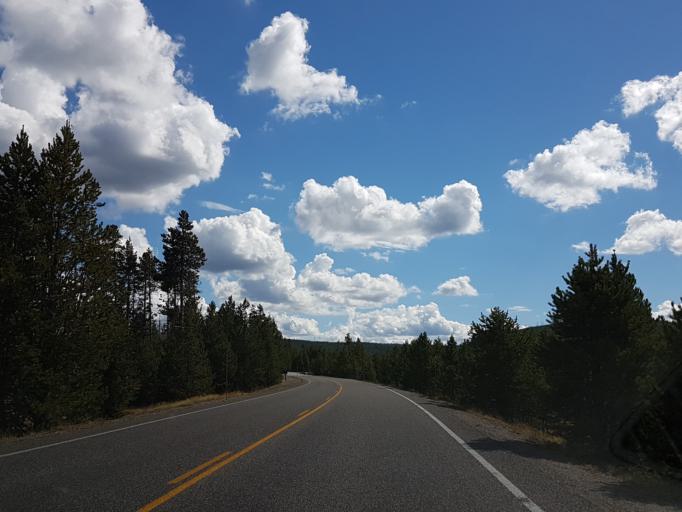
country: US
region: Montana
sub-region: Gallatin County
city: West Yellowstone
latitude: 44.4654
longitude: -110.8539
